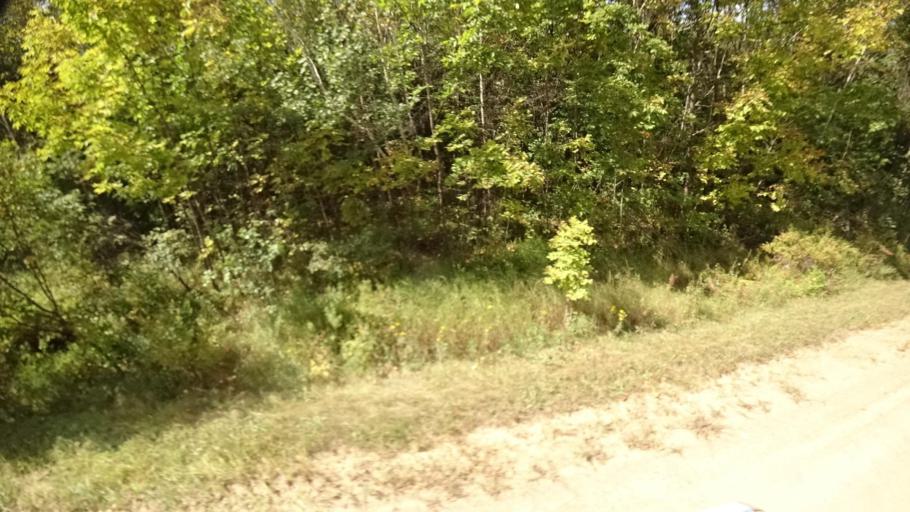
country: RU
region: Primorskiy
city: Yakovlevka
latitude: 44.7037
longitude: 133.6420
